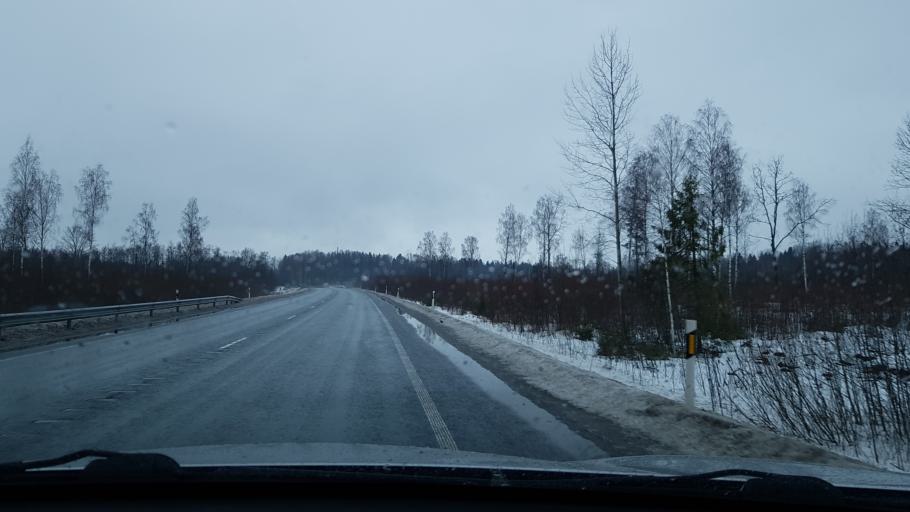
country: EE
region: Raplamaa
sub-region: Kohila vald
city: Kohila
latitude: 59.1349
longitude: 24.7922
